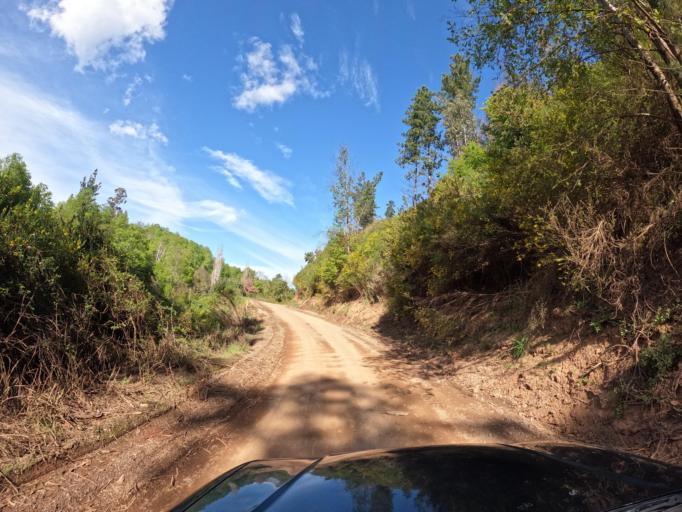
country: CL
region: Biobio
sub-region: Provincia de Concepcion
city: Chiguayante
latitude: -37.0724
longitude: -72.8425
